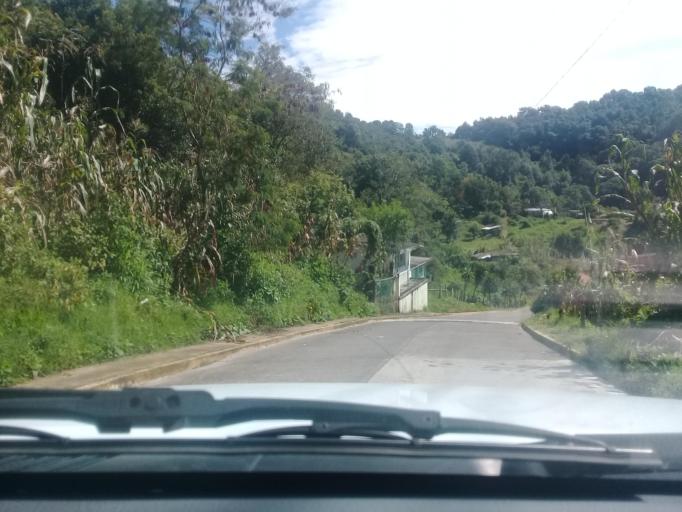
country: MX
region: Veracruz
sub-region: Tlalnelhuayocan
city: Otilpan
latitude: 19.5675
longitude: -96.9888
